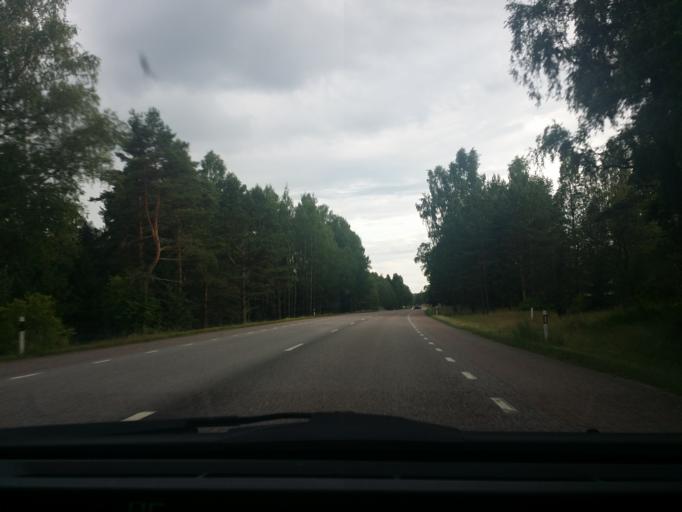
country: SE
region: OErebro
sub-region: Nora Kommun
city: Nora
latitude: 59.4536
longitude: 15.1352
